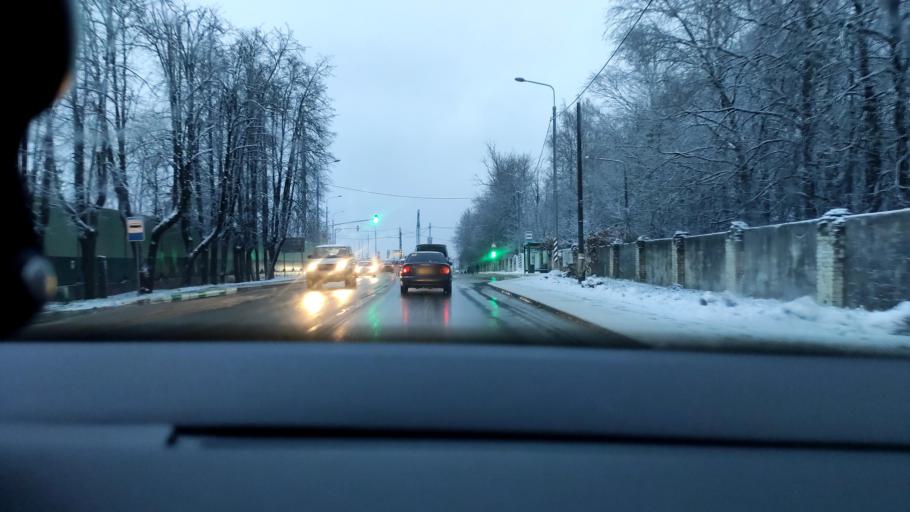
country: RU
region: Moskovskaya
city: Kubinka
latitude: 55.5624
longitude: 36.6990
